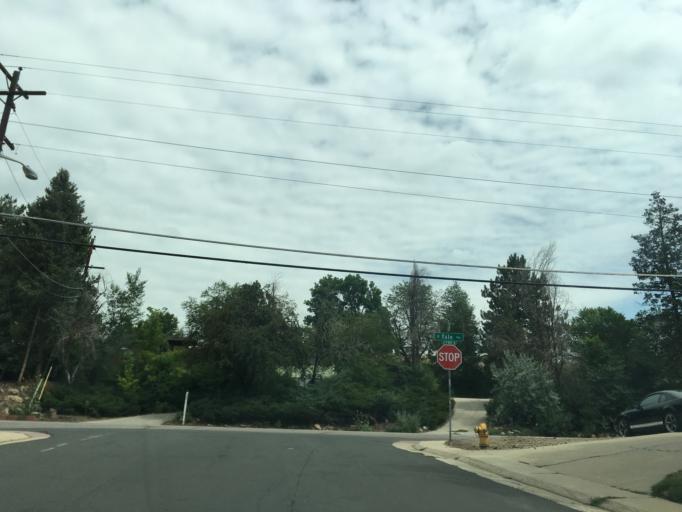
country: US
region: Colorado
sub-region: Arapahoe County
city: Sheridan
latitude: 39.6675
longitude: -105.0508
